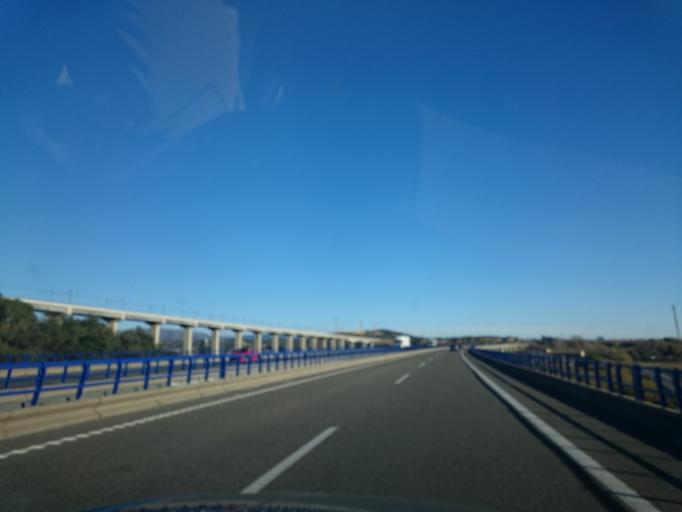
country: ES
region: Catalonia
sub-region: Provincia de Tarragona
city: Amposta
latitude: 40.7243
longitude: 0.5675
